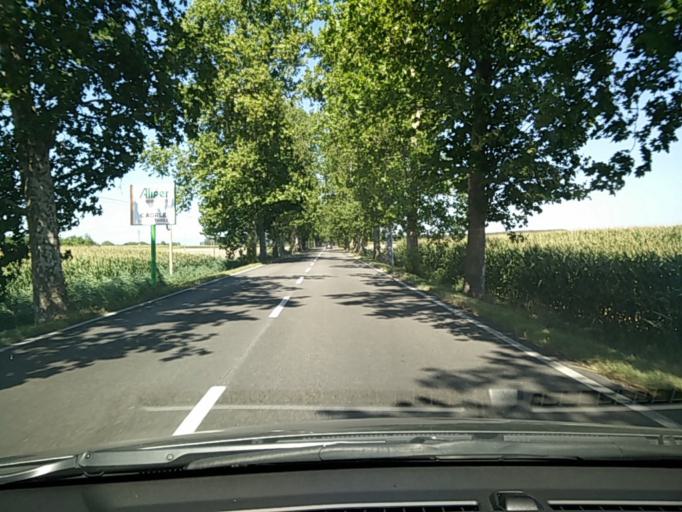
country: IT
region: Veneto
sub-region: Provincia di Venezia
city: La Salute di Livenza
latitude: 45.6721
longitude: 12.8095
